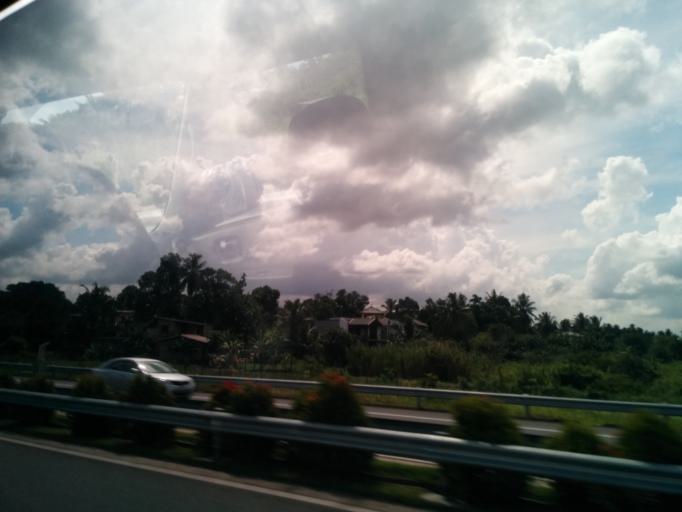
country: LK
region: Western
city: Wattala
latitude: 6.9729
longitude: 79.8941
